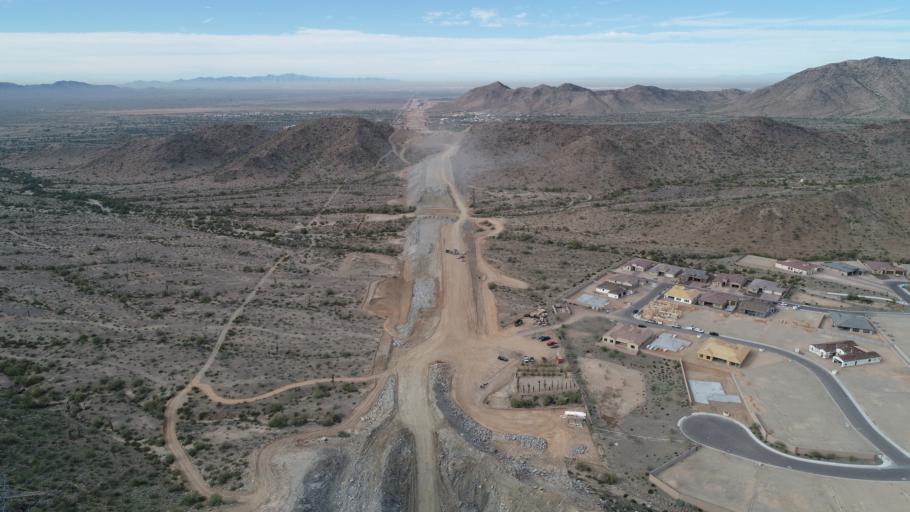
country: US
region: Arizona
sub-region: Maricopa County
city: Laveen
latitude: 33.2957
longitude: -112.1367
